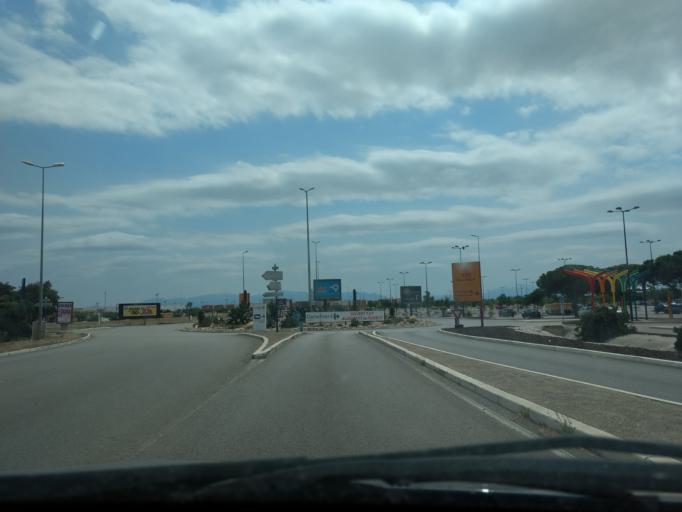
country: FR
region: Languedoc-Roussillon
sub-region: Departement des Pyrenees-Orientales
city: Pia
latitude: 42.7765
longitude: 2.9157
